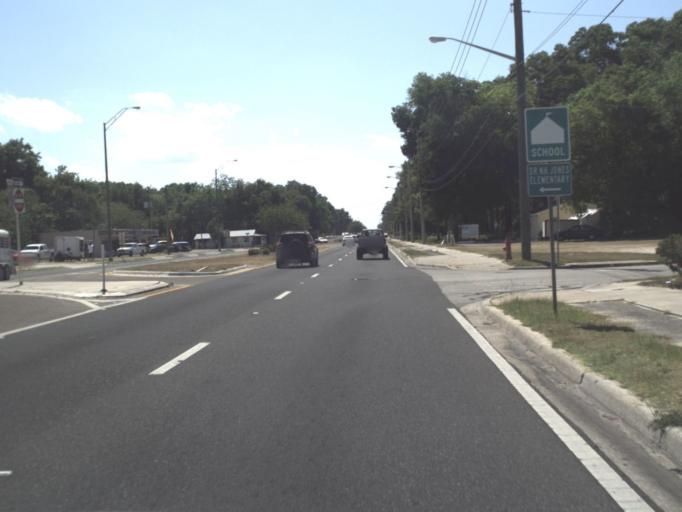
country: US
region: Florida
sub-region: Marion County
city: Ocala
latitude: 29.1863
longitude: -82.1581
